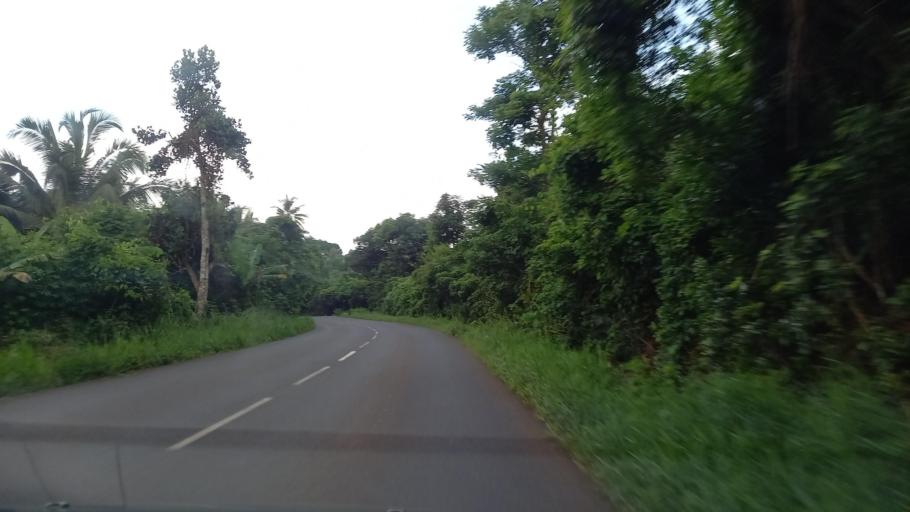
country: YT
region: M'Tsangamouji
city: M'Tsangamouji
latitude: -12.7629
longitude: 45.1042
